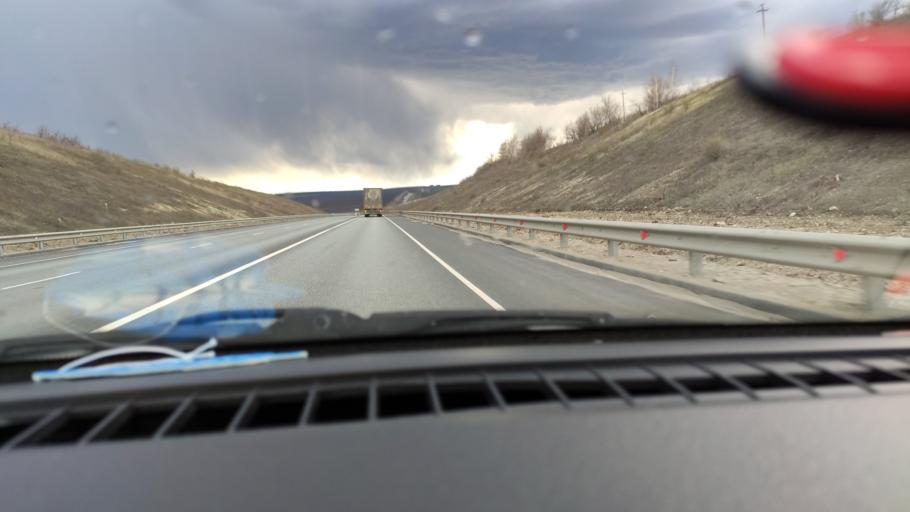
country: RU
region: Saratov
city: Yelshanka
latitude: 51.8837
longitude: 46.5133
